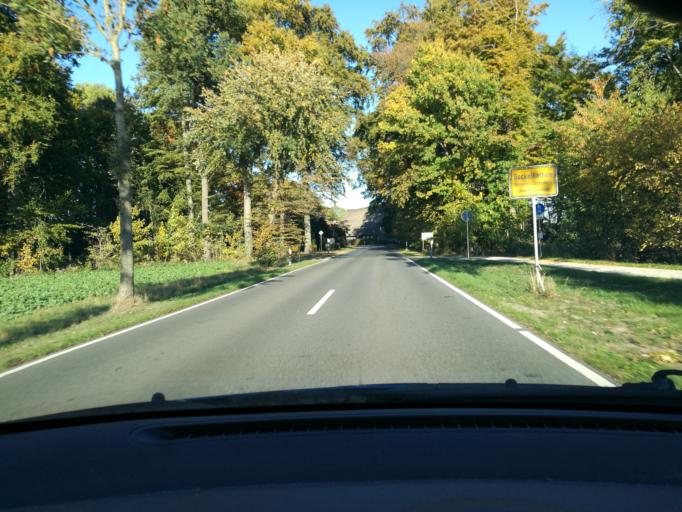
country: DE
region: Lower Saxony
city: Ludersburg
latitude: 53.3015
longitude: 10.5671
